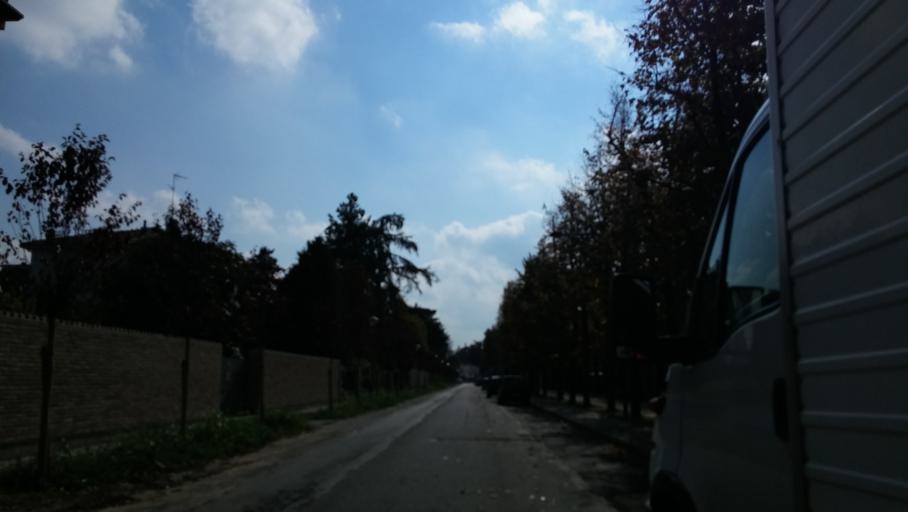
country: IT
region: Emilia-Romagna
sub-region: Provincia di Ferrara
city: Cento
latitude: 44.7292
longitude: 11.2859
